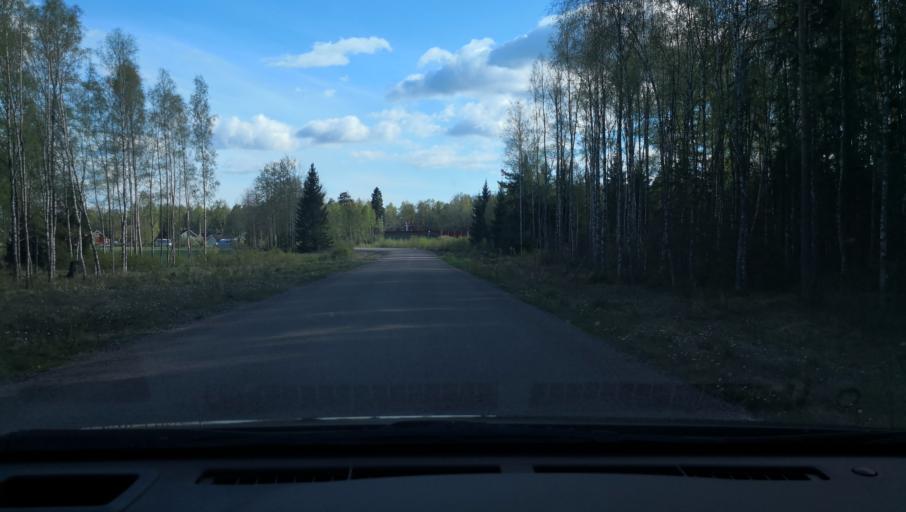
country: SE
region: OErebro
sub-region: Askersunds Kommun
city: Asbro
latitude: 58.9245
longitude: 15.0516
